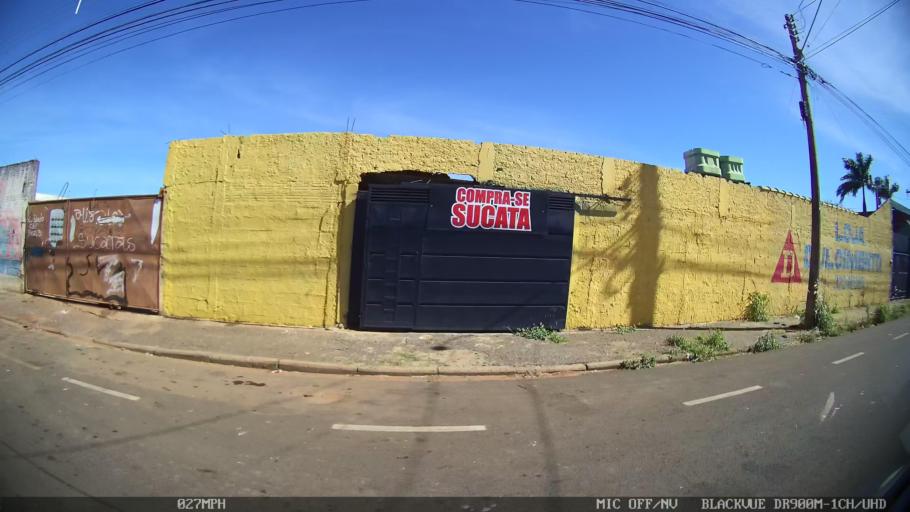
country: BR
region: Sao Paulo
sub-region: Franca
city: Franca
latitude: -20.5458
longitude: -47.3903
